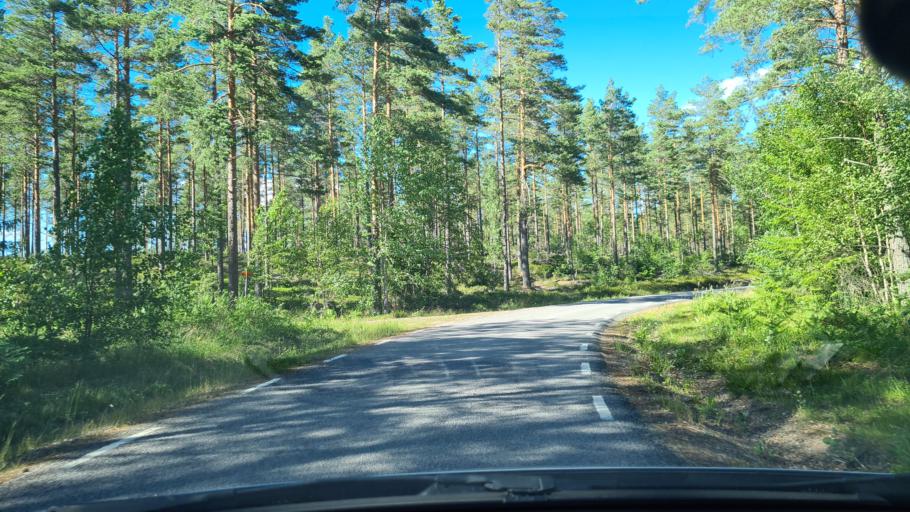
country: SE
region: OEstergoetland
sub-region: Norrkopings Kommun
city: Krokek
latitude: 58.7088
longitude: 16.4246
